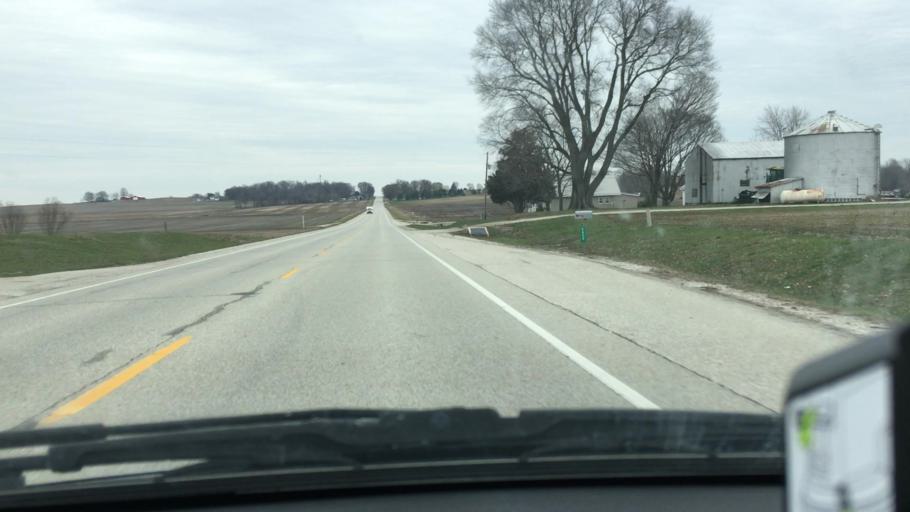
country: US
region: Indiana
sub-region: Greene County
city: Bloomfield
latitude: 38.9803
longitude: -87.0164
